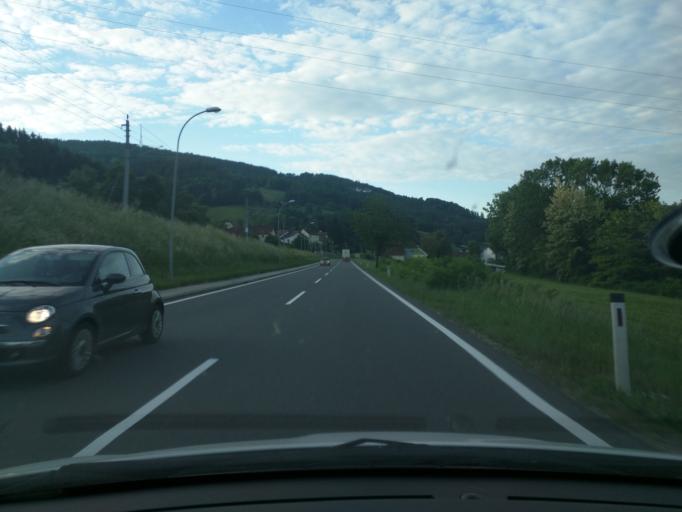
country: AT
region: Lower Austria
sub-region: Politischer Bezirk Amstetten
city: Sonntagberg
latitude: 48.0027
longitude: 14.7370
